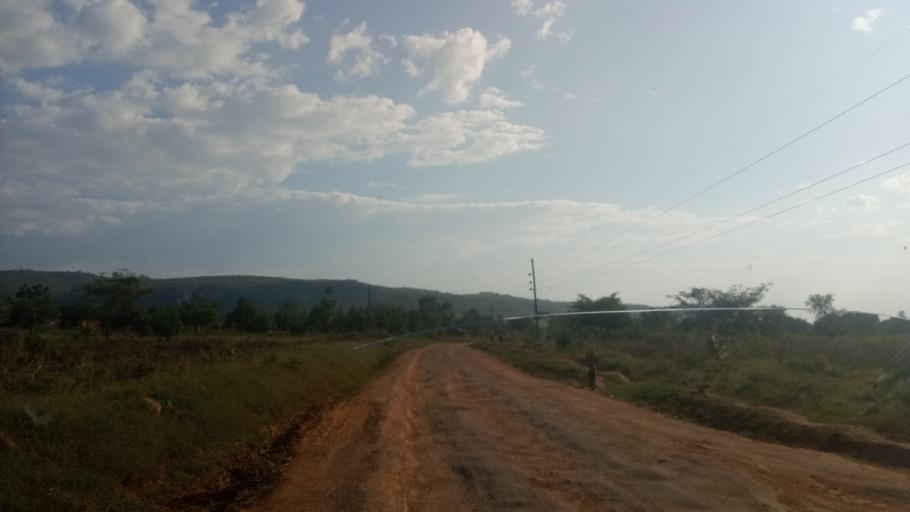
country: UG
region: Eastern Region
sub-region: Kapchorwa District
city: Kapchorwa
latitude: 1.4098
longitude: 34.3477
